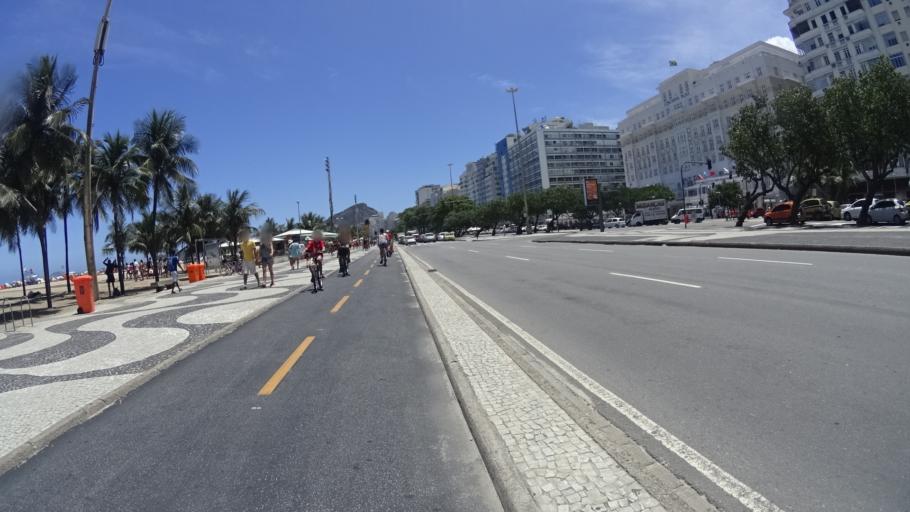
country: BR
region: Rio de Janeiro
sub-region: Rio De Janeiro
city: Rio de Janeiro
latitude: -22.9674
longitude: -43.1776
